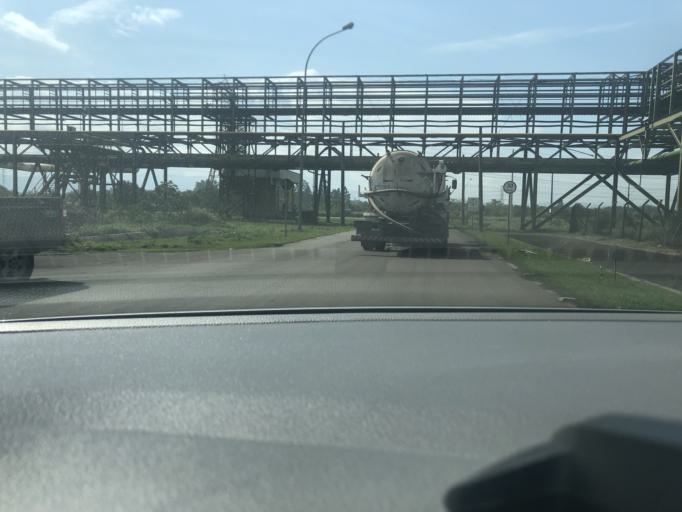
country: BR
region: Rio de Janeiro
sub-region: Itaguai
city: Itaguai
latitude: -22.9131
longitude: -43.7469
